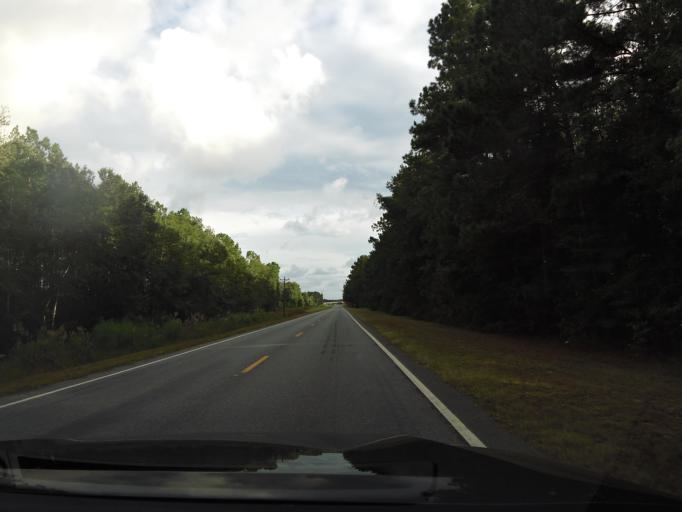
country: US
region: Georgia
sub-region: Liberty County
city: Midway
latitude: 31.6638
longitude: -81.3988
